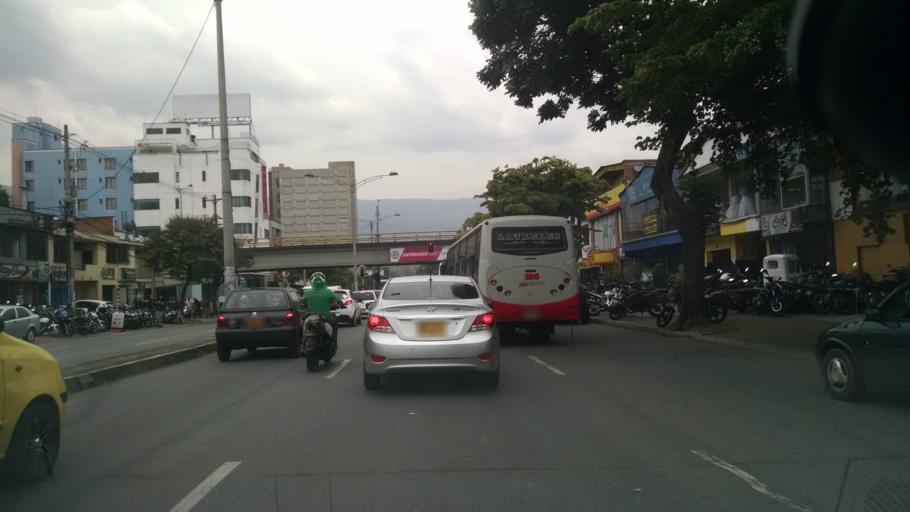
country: CO
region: Antioquia
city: Medellin
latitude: 6.2394
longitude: -75.5838
